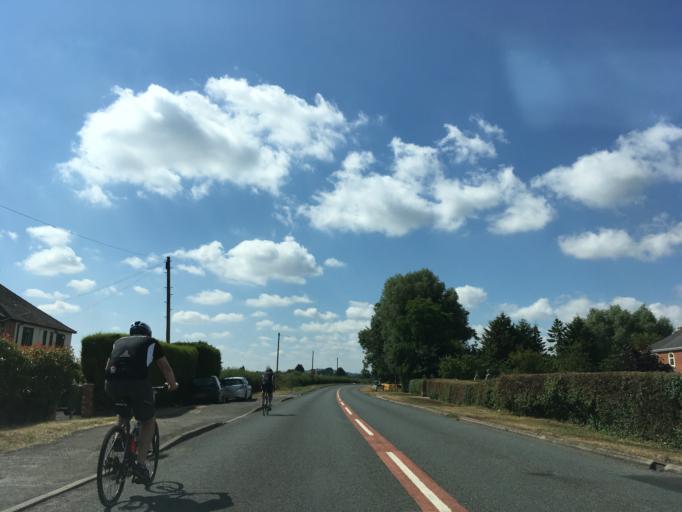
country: GB
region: England
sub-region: Gloucestershire
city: Barnwood
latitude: 51.9059
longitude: -2.2132
